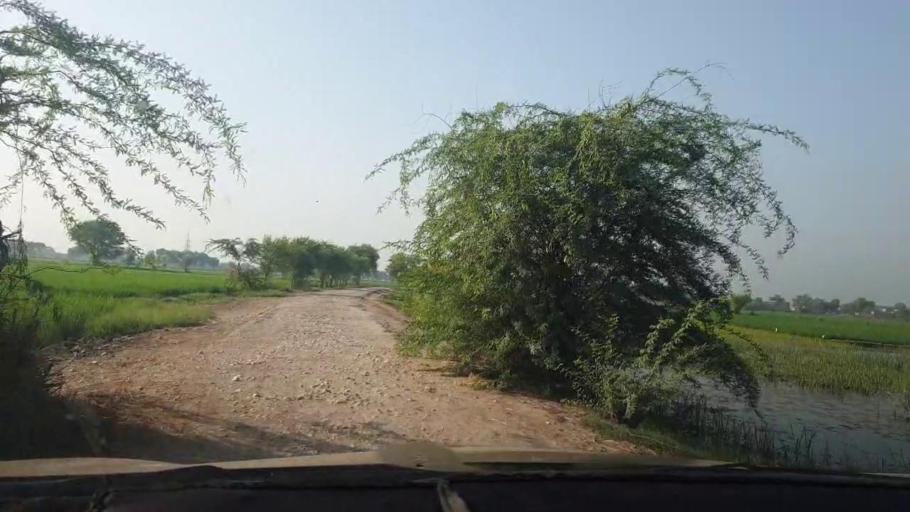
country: PK
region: Sindh
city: Kambar
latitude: 27.5765
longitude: 68.1025
